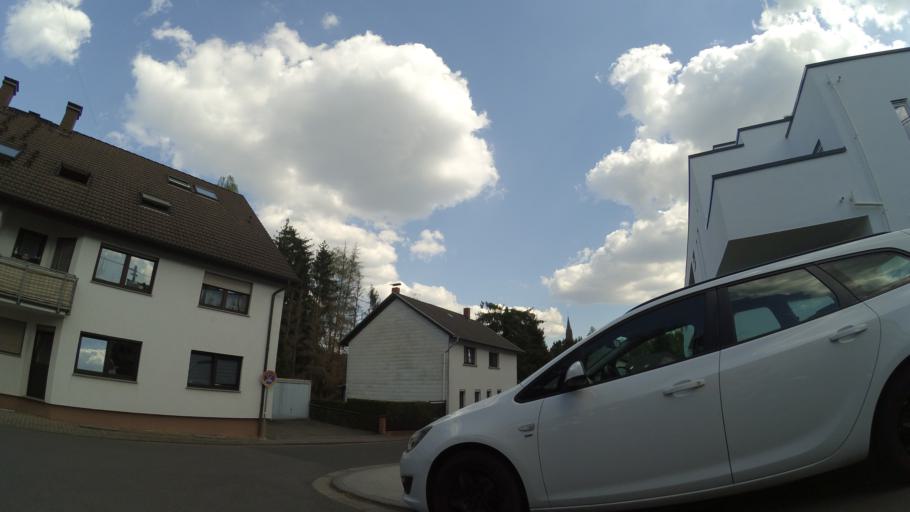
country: DE
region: Saarland
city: Riegelsberg
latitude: 49.3098
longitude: 6.9379
